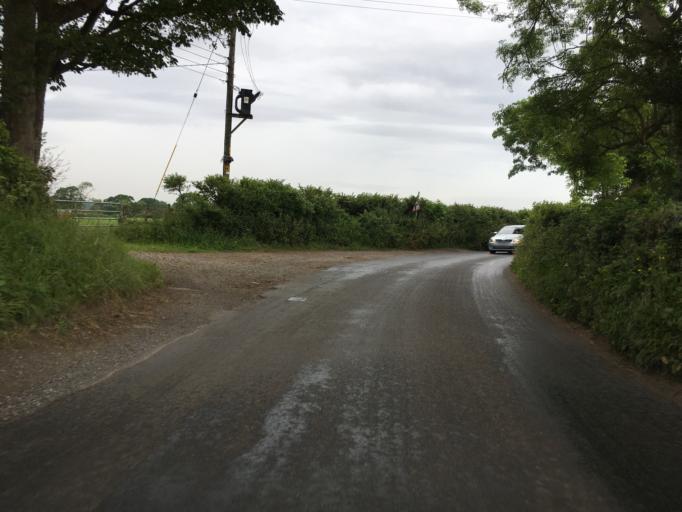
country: GB
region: England
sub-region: North Somerset
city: Brockley
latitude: 51.4138
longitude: -2.7886
